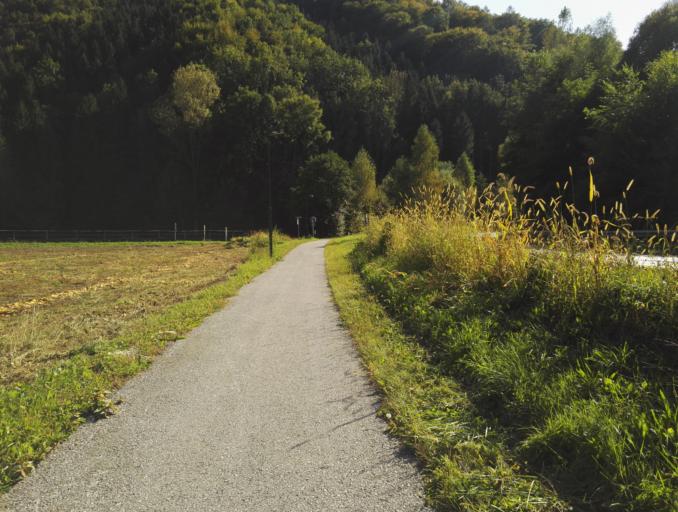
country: AT
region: Styria
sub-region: Politischer Bezirk Graz-Umgebung
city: Peggau
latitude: 47.1920
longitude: 15.3467
